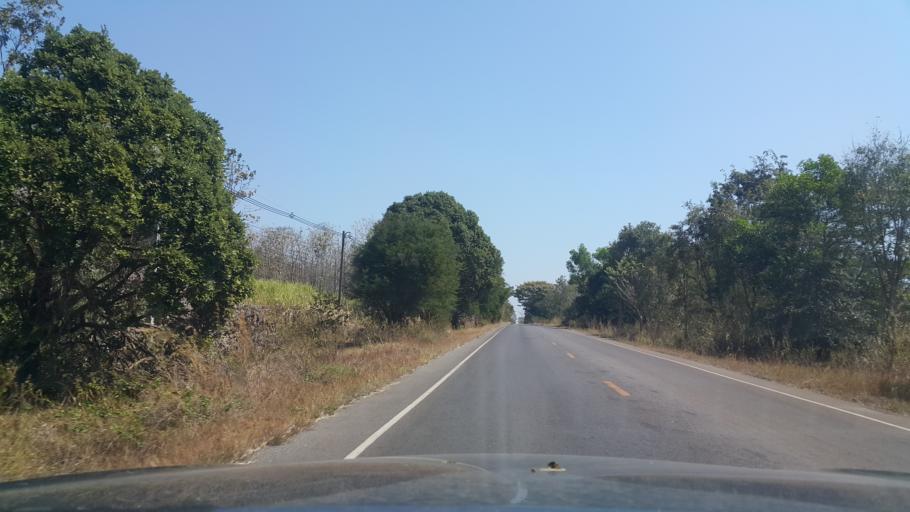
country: TH
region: Changwat Udon Thani
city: Ban Dung
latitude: 17.6084
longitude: 103.2605
